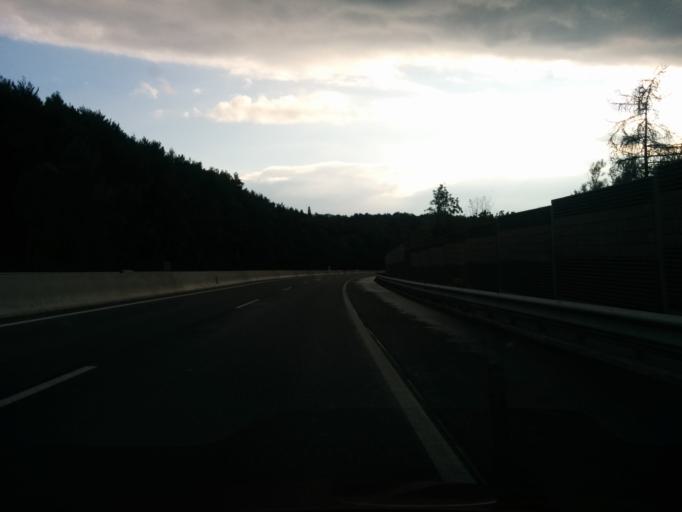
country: AT
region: Lower Austria
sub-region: Politischer Bezirk Sankt Polten
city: Eichgraben
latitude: 48.1556
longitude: 15.9886
